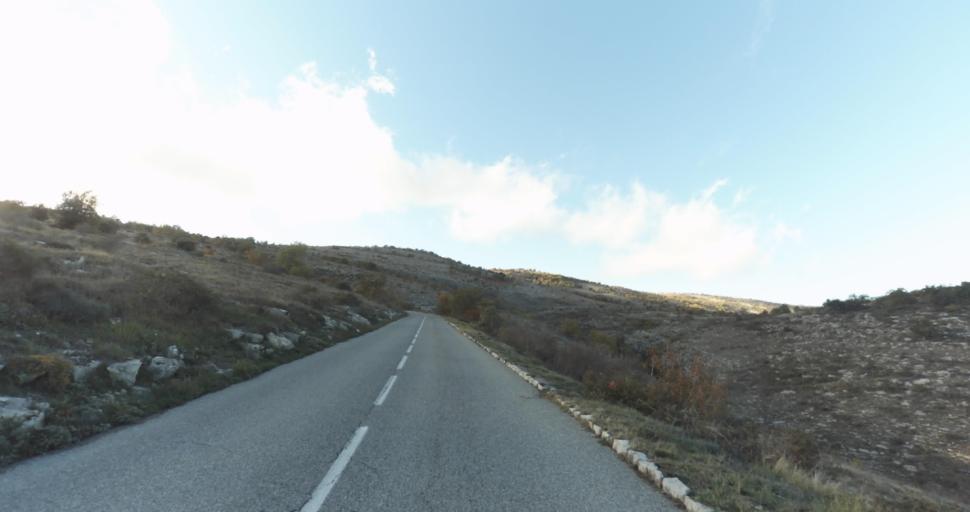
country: FR
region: Provence-Alpes-Cote d'Azur
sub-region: Departement des Alpes-Maritimes
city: Vence
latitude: 43.7541
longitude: 7.0906
